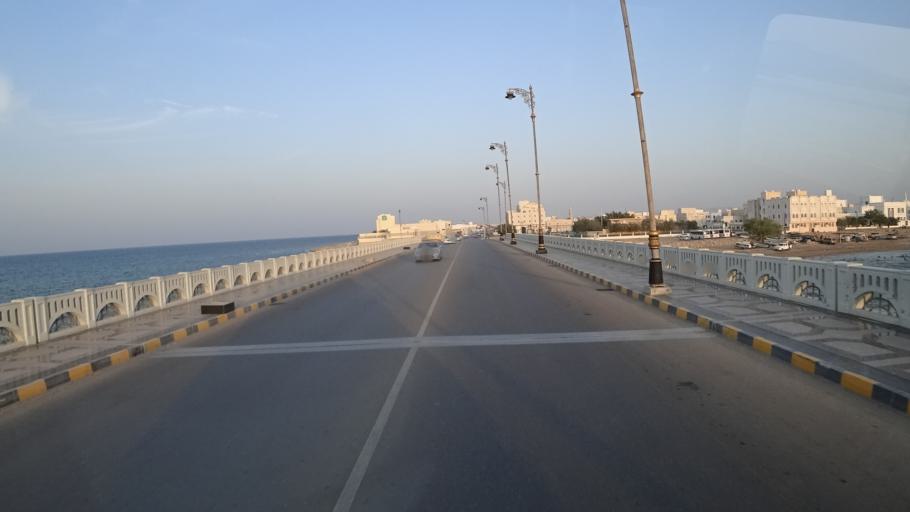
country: OM
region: Ash Sharqiyah
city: Sur
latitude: 22.5967
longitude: 59.4904
